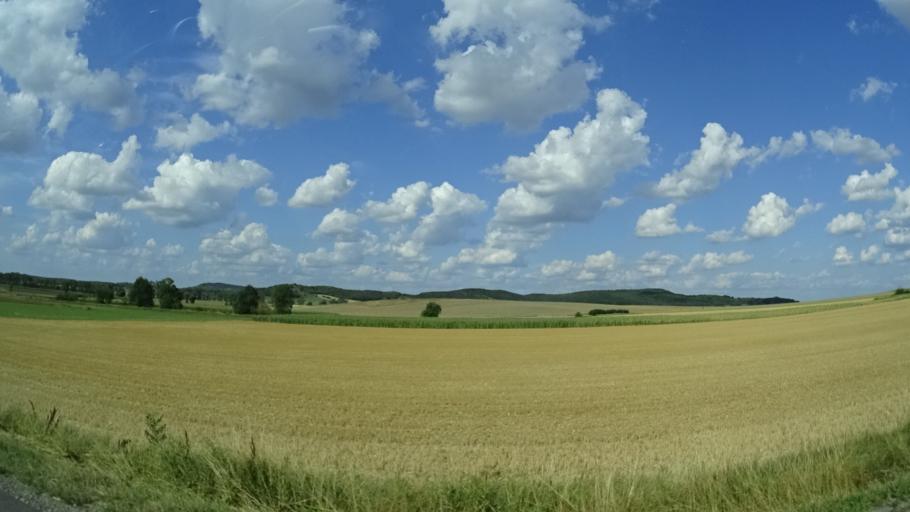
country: DE
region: Bavaria
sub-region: Regierungsbezirk Unterfranken
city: Bad Konigshofen im Grabfeld
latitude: 50.2812
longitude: 10.4923
